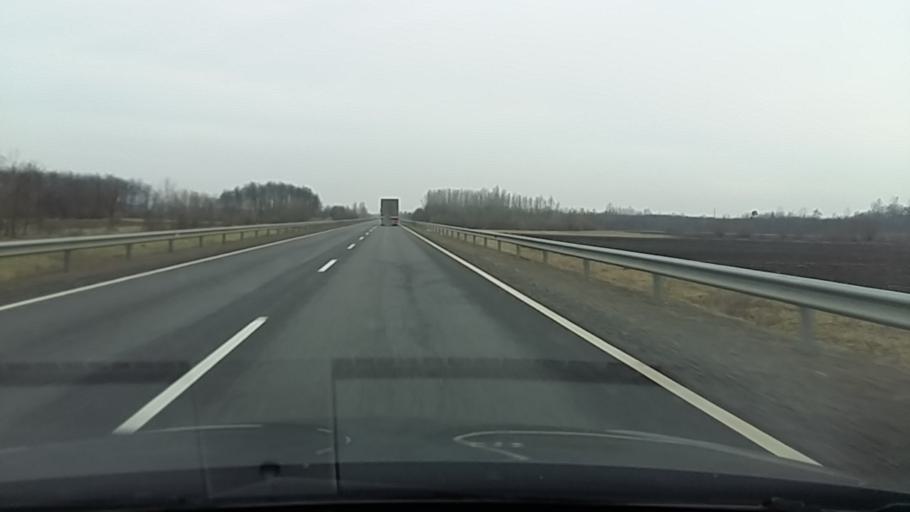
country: HU
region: Szabolcs-Szatmar-Bereg
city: Nyirpazony
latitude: 47.9771
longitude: 21.8182
